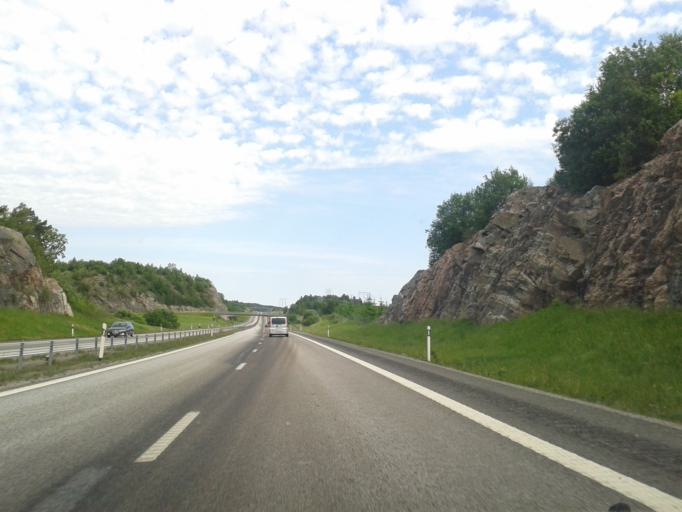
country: SE
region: Vaestra Goetaland
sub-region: Munkedals Kommun
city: Munkedal
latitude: 58.4982
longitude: 11.5702
